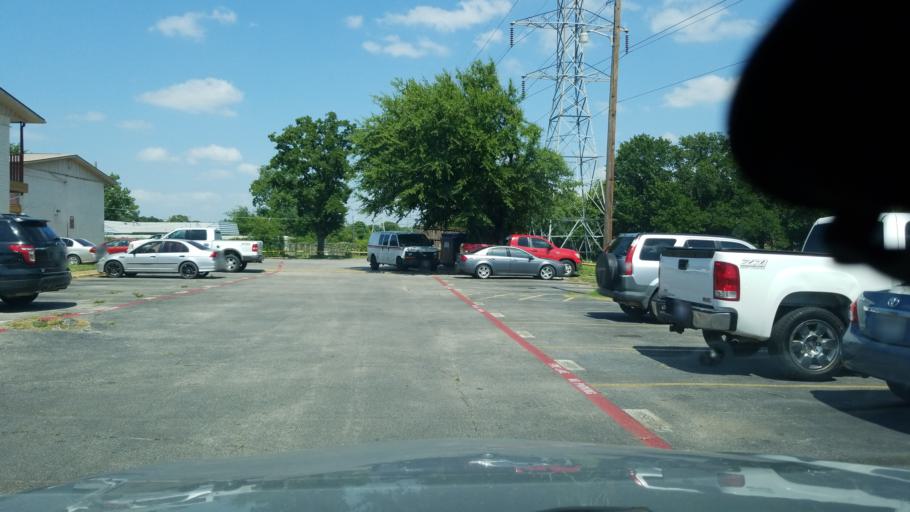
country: US
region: Texas
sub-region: Dallas County
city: Irving
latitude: 32.8175
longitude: -96.9550
